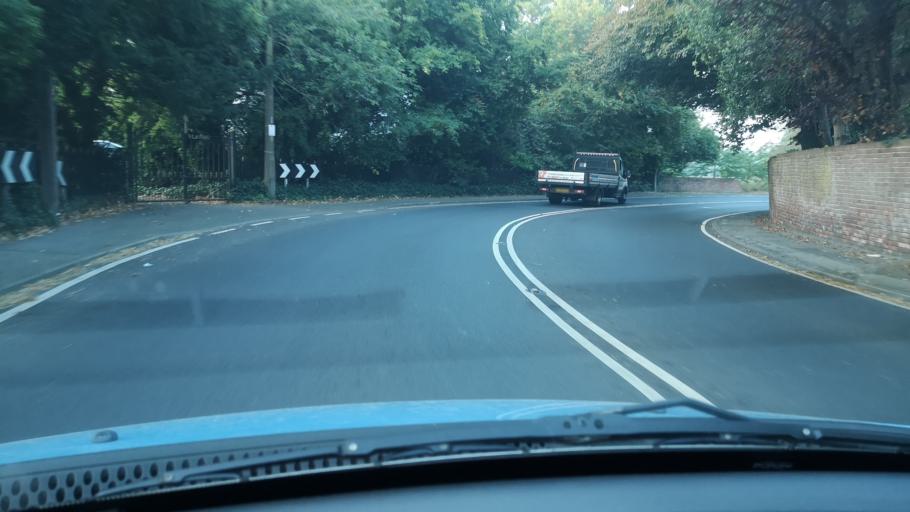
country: GB
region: England
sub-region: Doncaster
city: Hatfield
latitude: 53.5745
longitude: -1.0016
